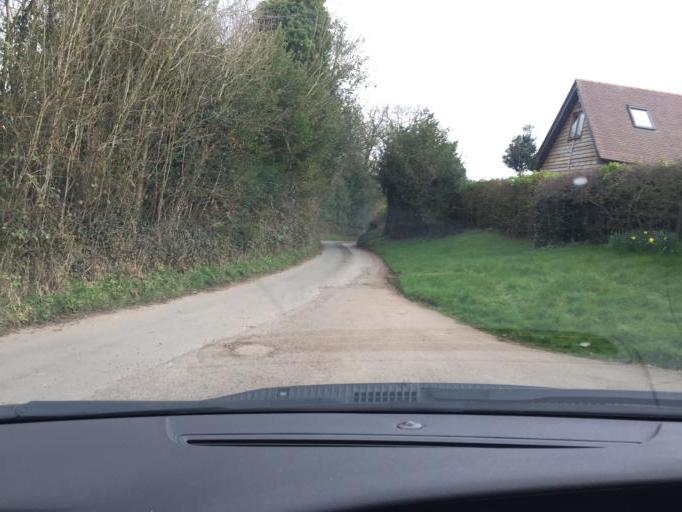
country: GB
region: England
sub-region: Solihull
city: Meriden
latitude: 52.4474
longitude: -1.5947
